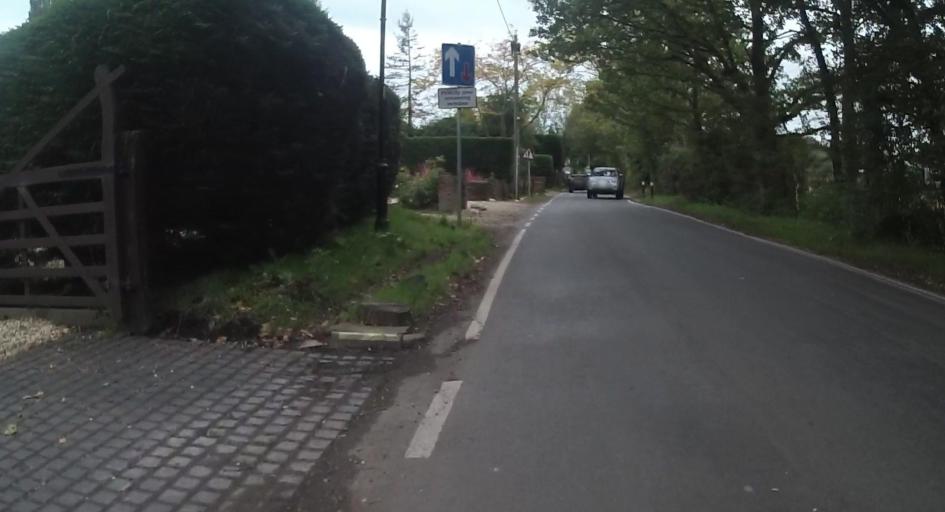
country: GB
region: England
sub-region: Hampshire
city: Fleet
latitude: 51.2619
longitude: -0.8666
